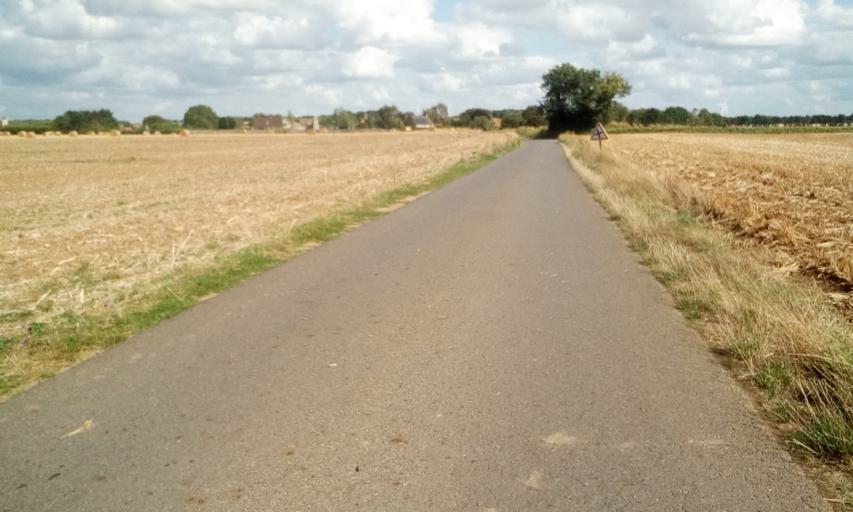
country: FR
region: Lower Normandy
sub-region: Departement du Calvados
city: Saint-Sylvain
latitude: 49.0884
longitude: -0.2051
